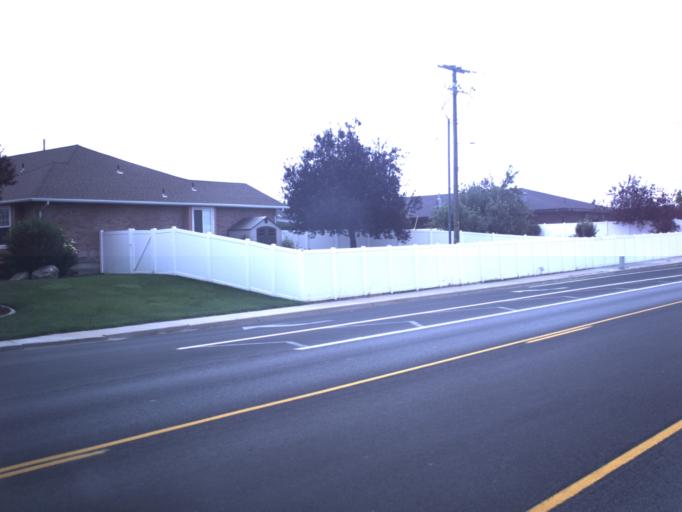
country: US
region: Utah
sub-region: Davis County
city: Clinton
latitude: 41.1358
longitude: -112.0645
